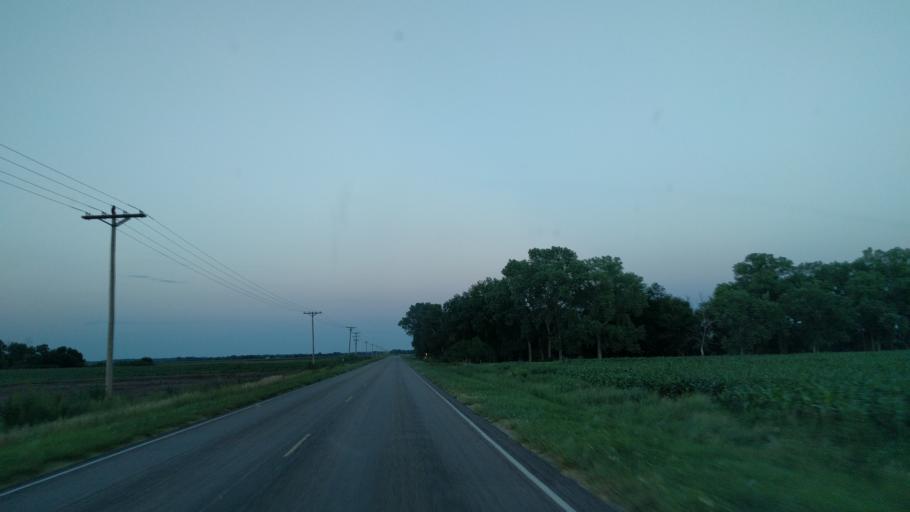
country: US
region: Kansas
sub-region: Reno County
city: Nickerson
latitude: 38.2176
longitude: -98.1059
